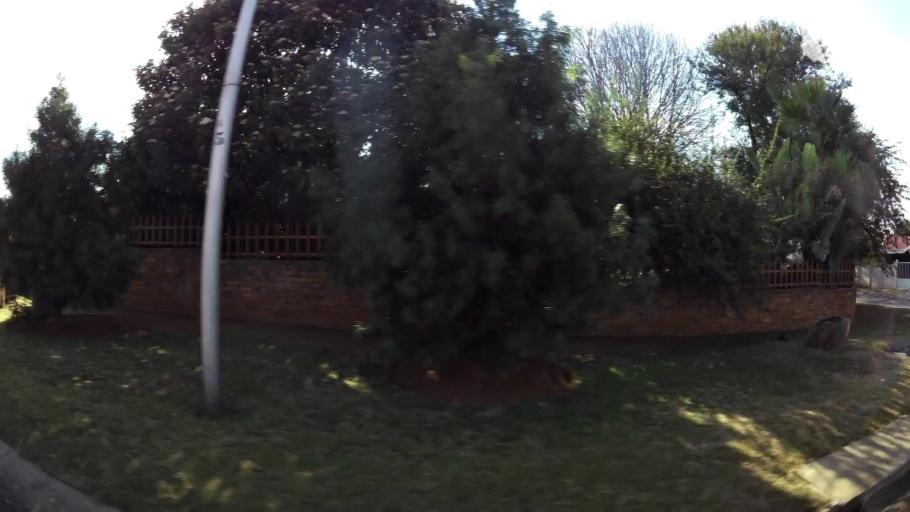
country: ZA
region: Gauteng
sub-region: Ekurhuleni Metropolitan Municipality
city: Benoni
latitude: -26.1405
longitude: 28.3499
